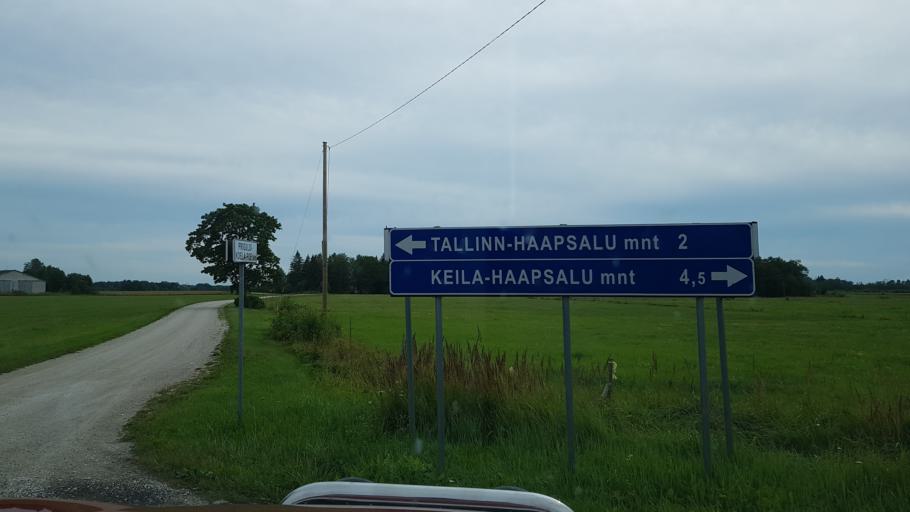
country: EE
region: Laeaene
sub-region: Ridala Parish
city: Uuemoisa
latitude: 58.9723
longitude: 23.7707
